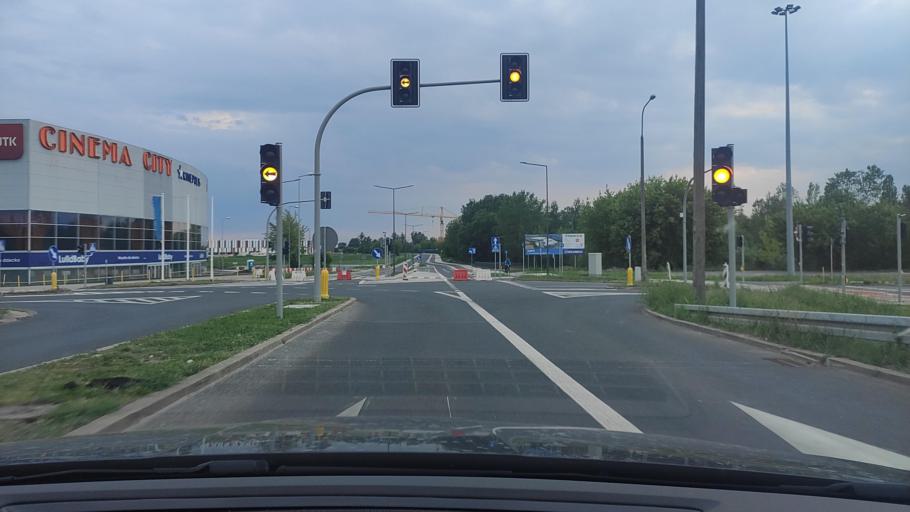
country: PL
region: Greater Poland Voivodeship
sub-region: Poznan
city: Poznan
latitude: 52.3754
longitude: 16.9812
